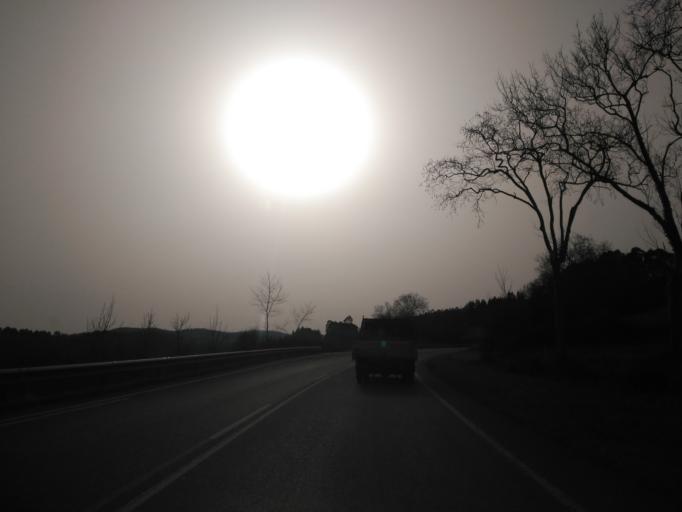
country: ES
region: Cantabria
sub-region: Provincia de Cantabria
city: Comillas
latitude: 43.3734
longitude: -4.2829
